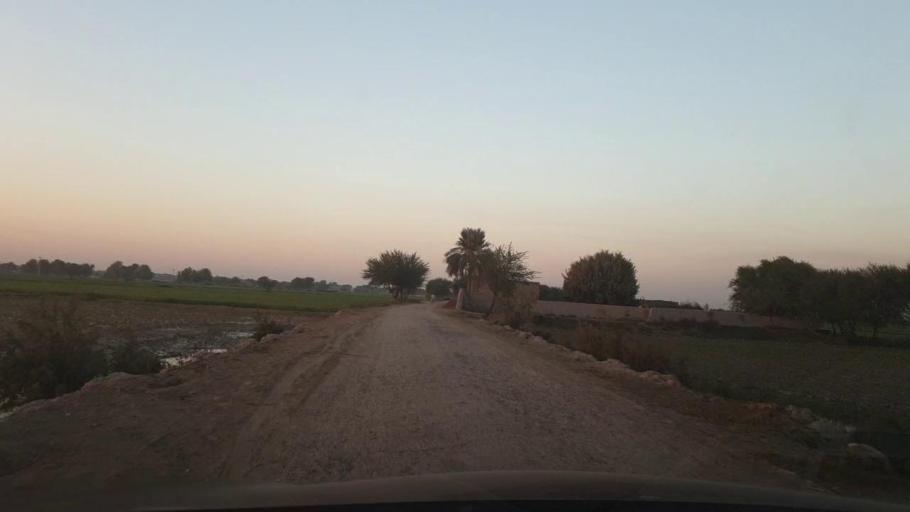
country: PK
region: Sindh
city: Ubauro
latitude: 28.1681
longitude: 69.6357
